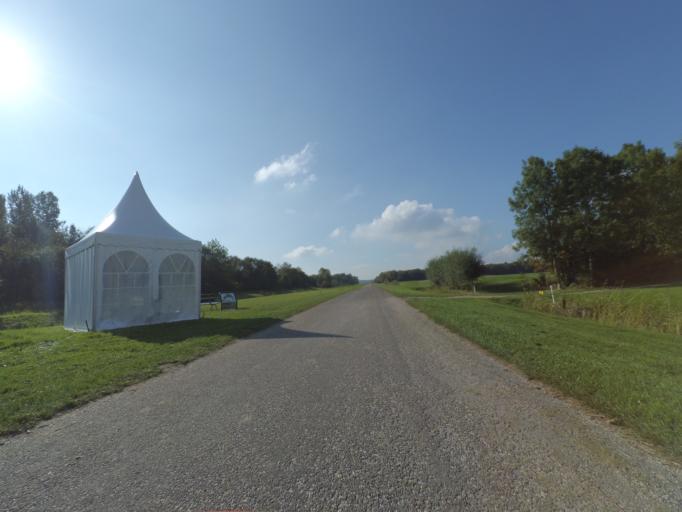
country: NL
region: Flevoland
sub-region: Gemeente Dronten
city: Biddinghuizen
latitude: 52.4086
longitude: 5.6744
